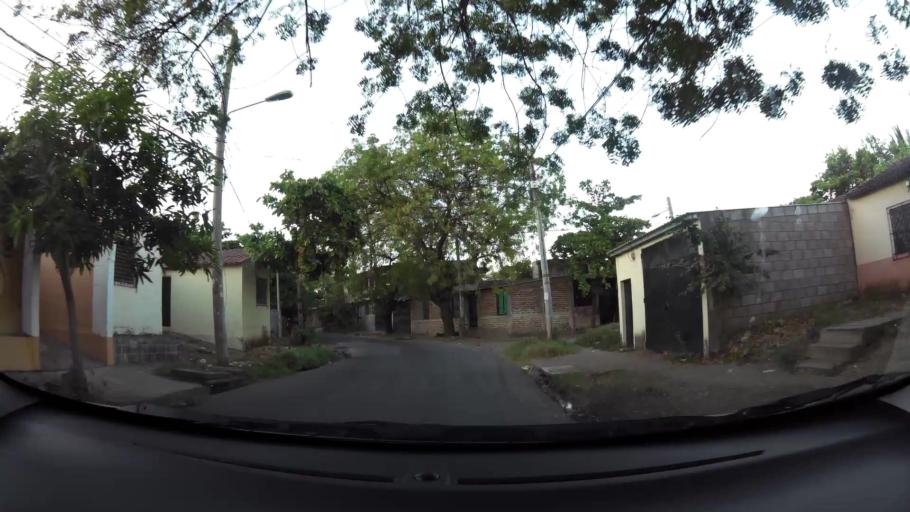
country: SV
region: San Miguel
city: San Miguel
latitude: 13.4809
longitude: -88.1579
